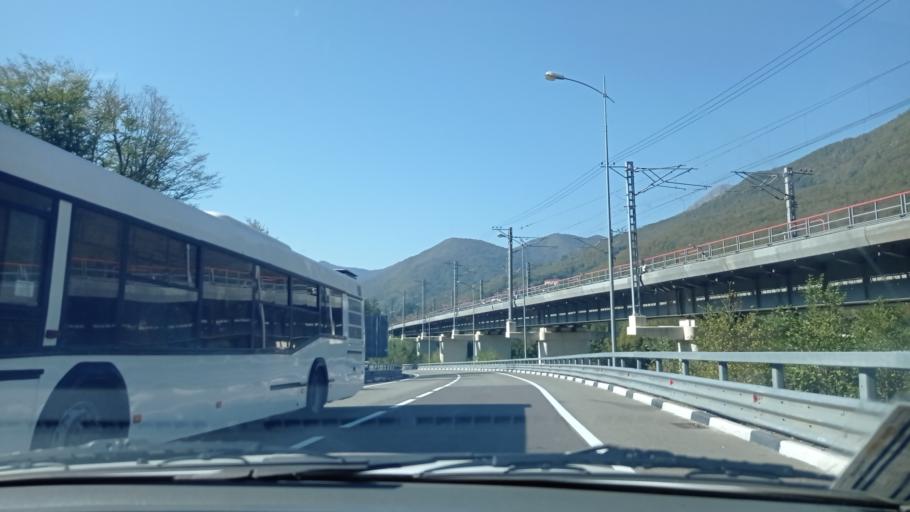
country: RU
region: Krasnodarskiy
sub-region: Sochi City
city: Krasnaya Polyana
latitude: 43.6841
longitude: 40.2444
